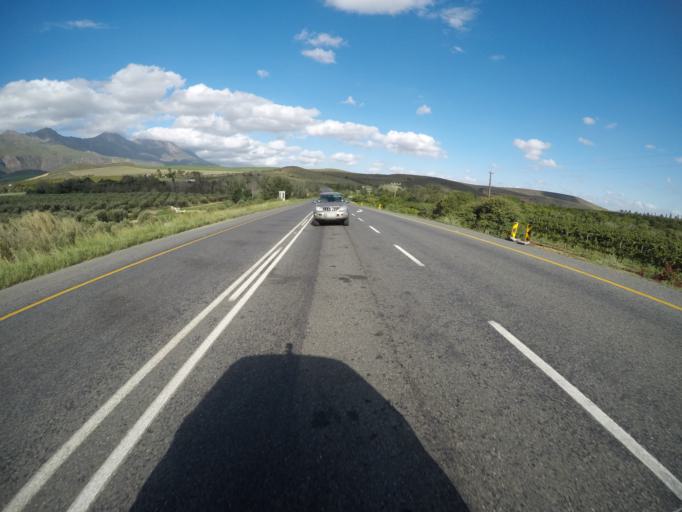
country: ZA
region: Western Cape
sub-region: Cape Winelands District Municipality
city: Ashton
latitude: -33.9473
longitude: 20.2167
